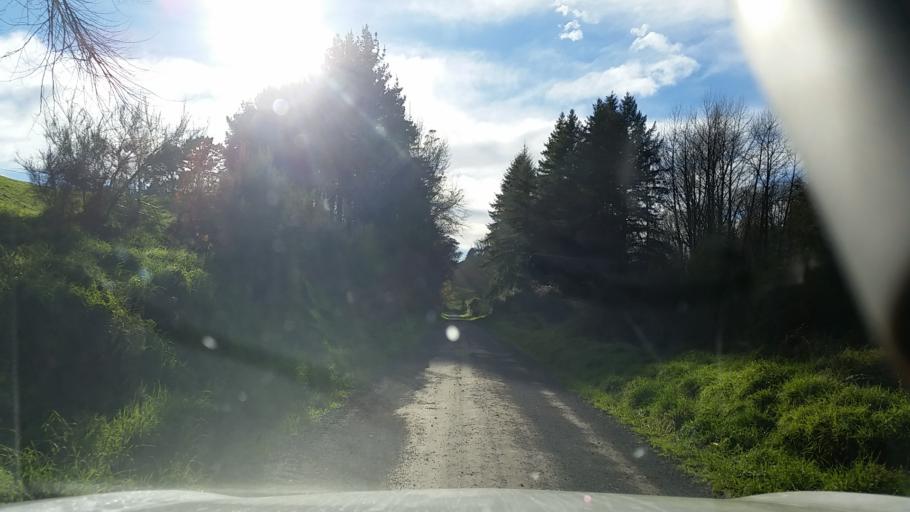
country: NZ
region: Waikato
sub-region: South Waikato District
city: Tokoroa
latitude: -38.3814
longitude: 176.0833
